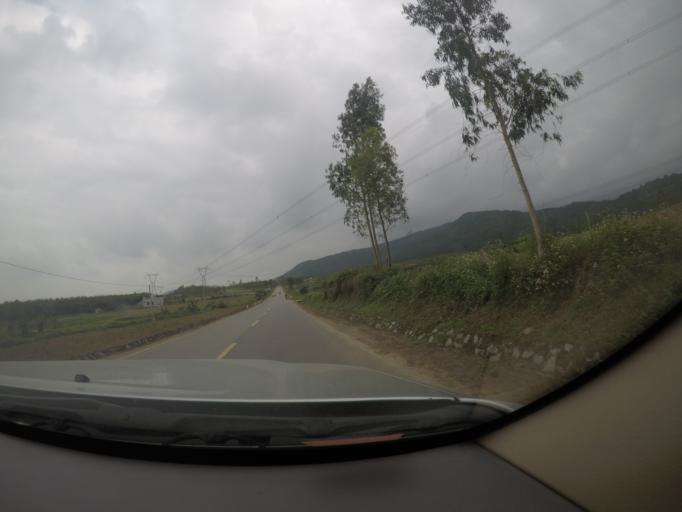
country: VN
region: Quang Binh
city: Hoan Lao
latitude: 17.5692
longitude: 106.4419
